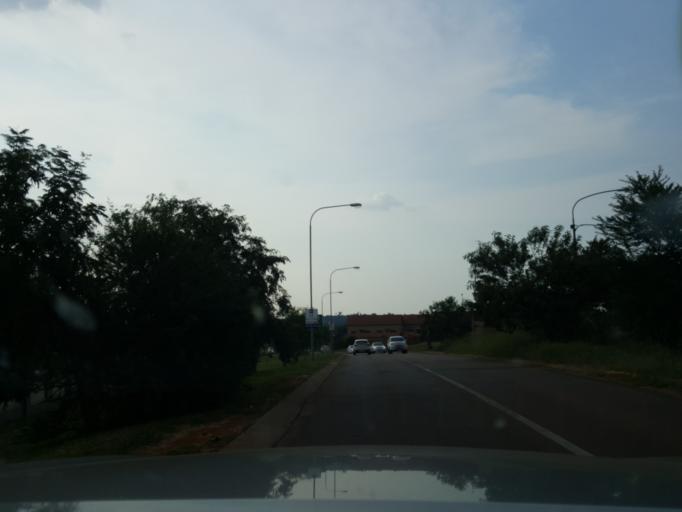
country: ZA
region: Gauteng
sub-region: City of Tshwane Metropolitan Municipality
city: Centurion
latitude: -25.8661
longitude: 28.2122
